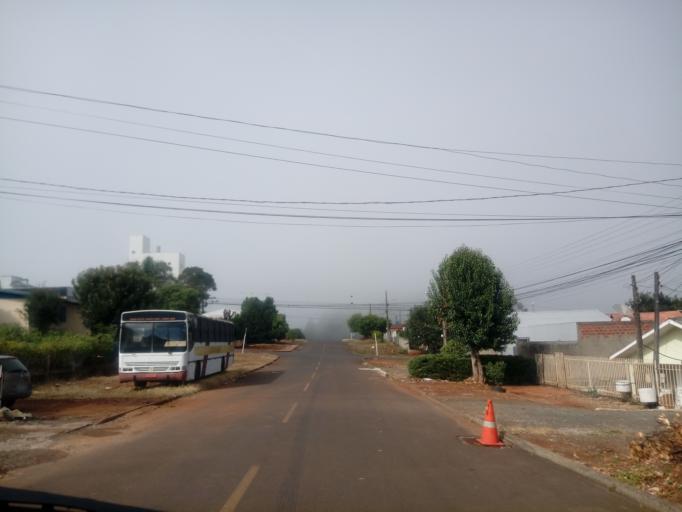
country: BR
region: Santa Catarina
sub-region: Chapeco
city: Chapeco
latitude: -27.0837
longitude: -52.6092
